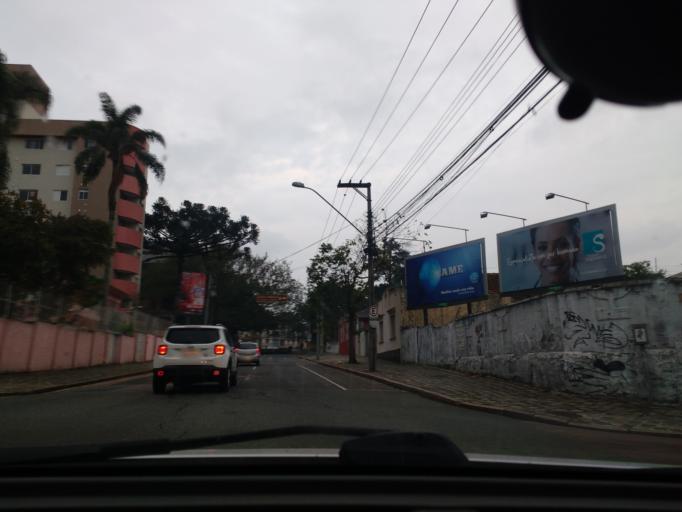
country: BR
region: Parana
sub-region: Curitiba
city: Curitiba
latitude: -25.4263
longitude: -49.2794
